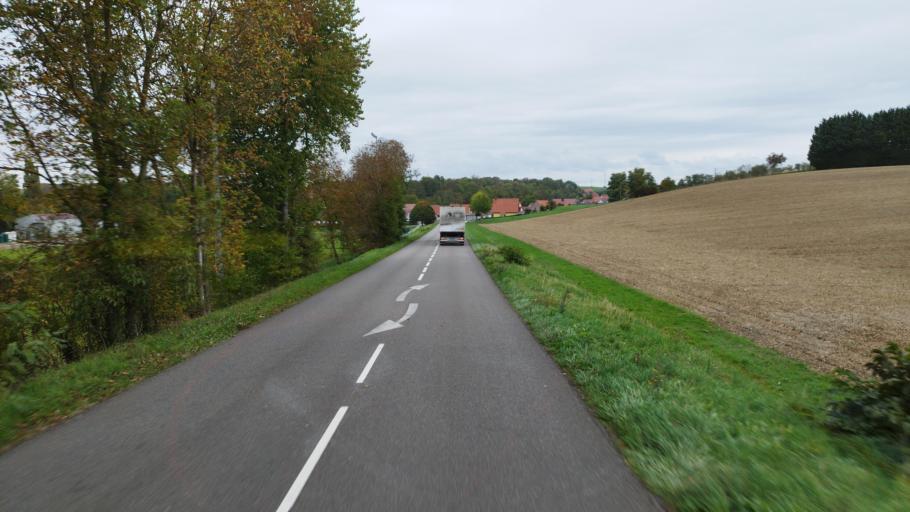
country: DE
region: Rheinland-Pfalz
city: Scheibenhardt
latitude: 48.9502
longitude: 8.1174
